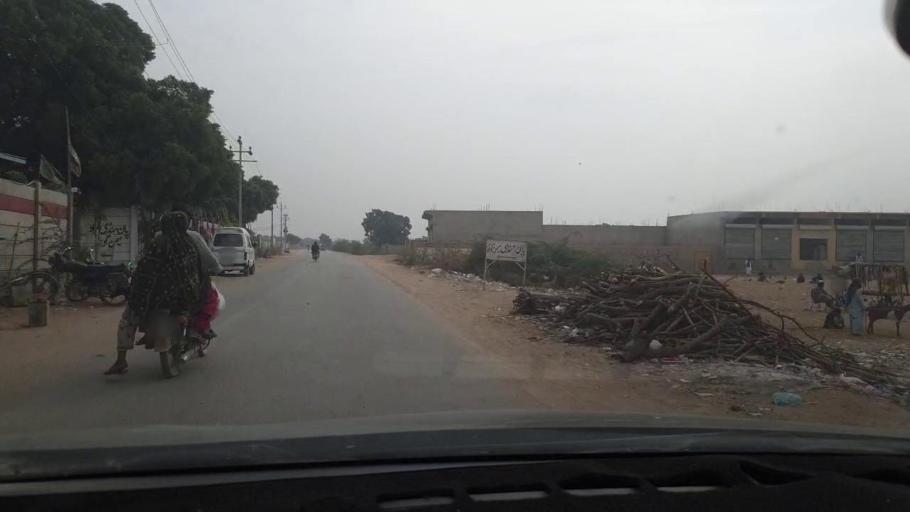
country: PK
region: Sindh
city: Malir Cantonment
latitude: 24.9185
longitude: 67.2586
